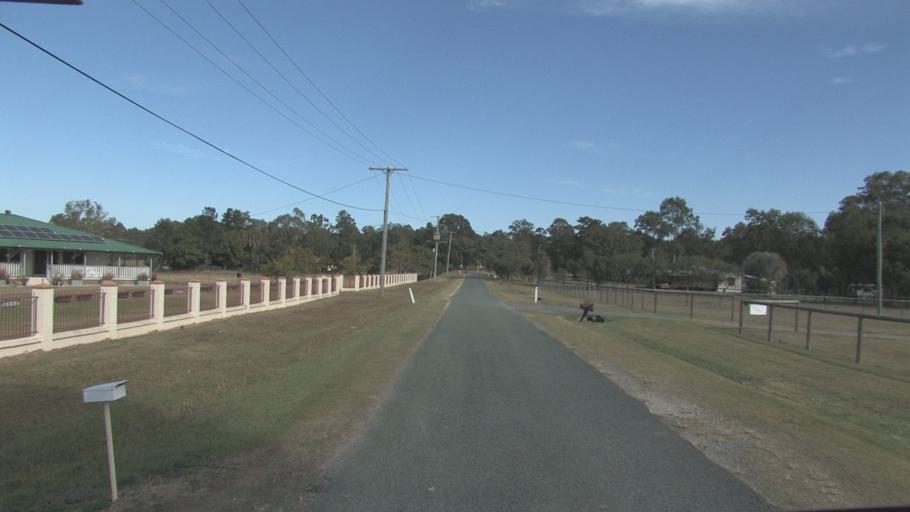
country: AU
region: Queensland
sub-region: Logan
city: North Maclean
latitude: -27.7755
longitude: 152.9967
